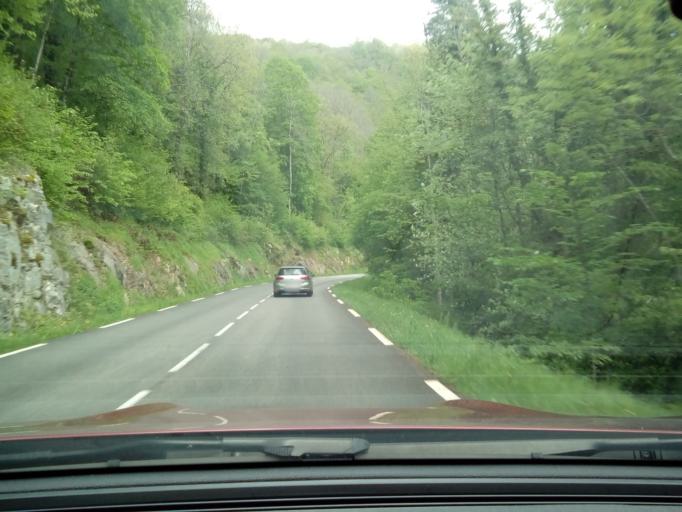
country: FR
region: Rhone-Alpes
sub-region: Departement de la Savoie
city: Barby
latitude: 45.6109
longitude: 6.0132
